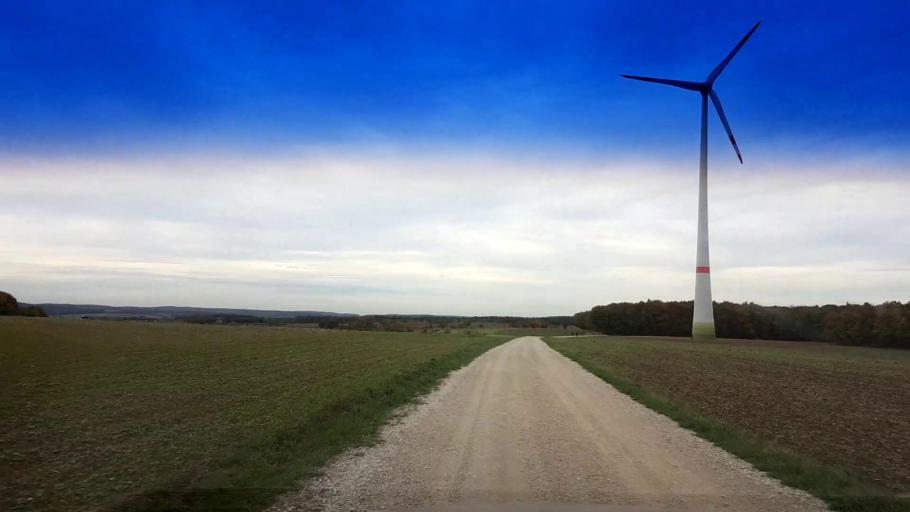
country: DE
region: Bavaria
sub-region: Upper Franconia
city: Priesendorf
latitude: 49.9102
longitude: 10.7356
